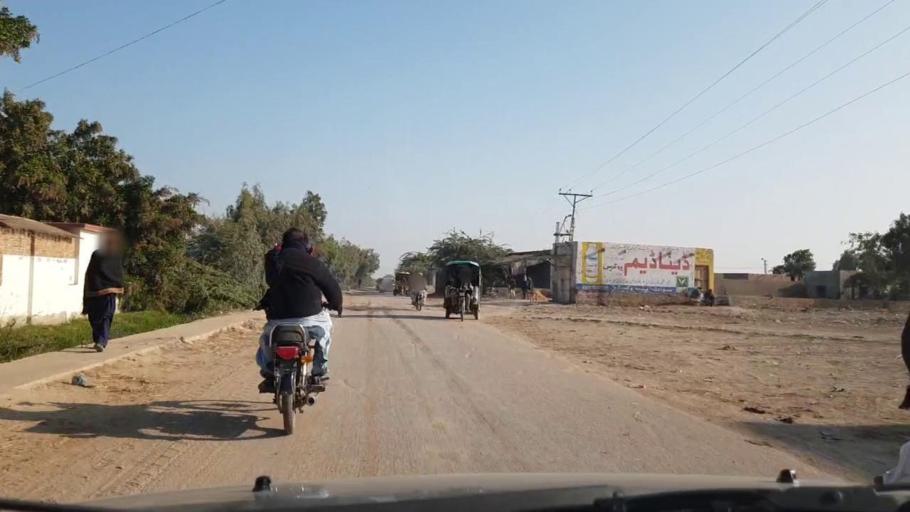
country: PK
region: Sindh
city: Tando Bago
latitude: 24.7905
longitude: 68.9714
